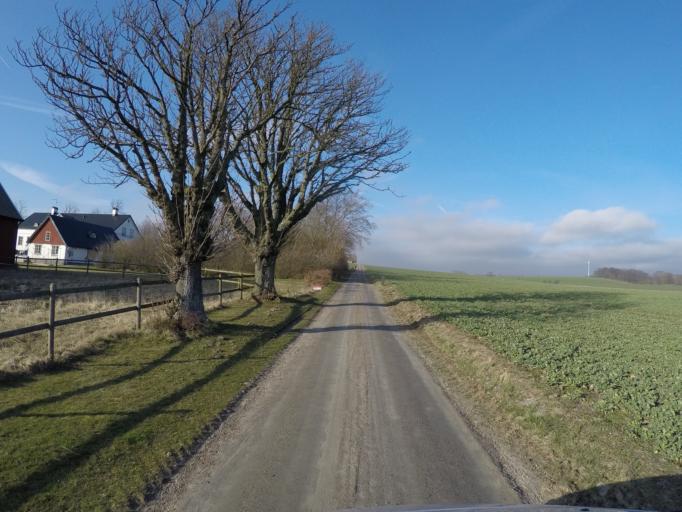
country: SE
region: Skane
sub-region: Staffanstorps Kommun
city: Staffanstorp
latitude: 55.6886
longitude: 13.2698
